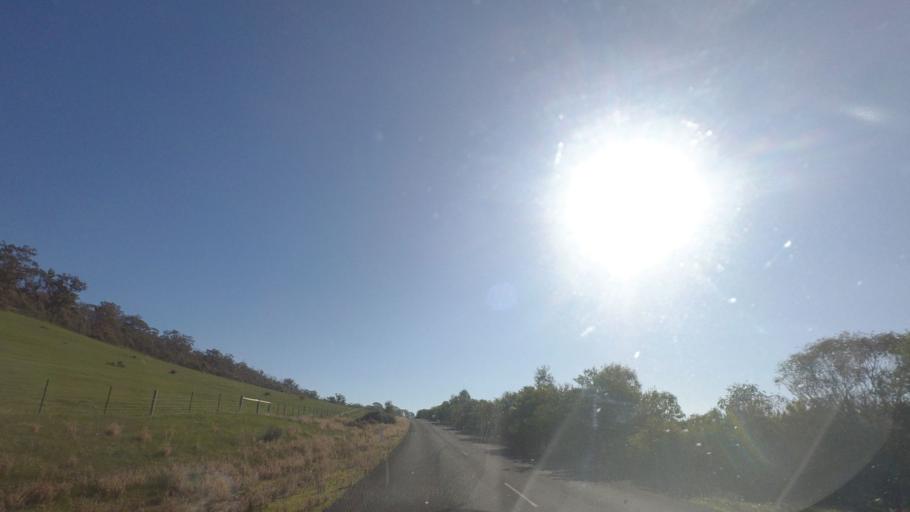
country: AU
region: Victoria
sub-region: Mount Alexander
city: Castlemaine
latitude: -37.0388
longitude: 144.2786
